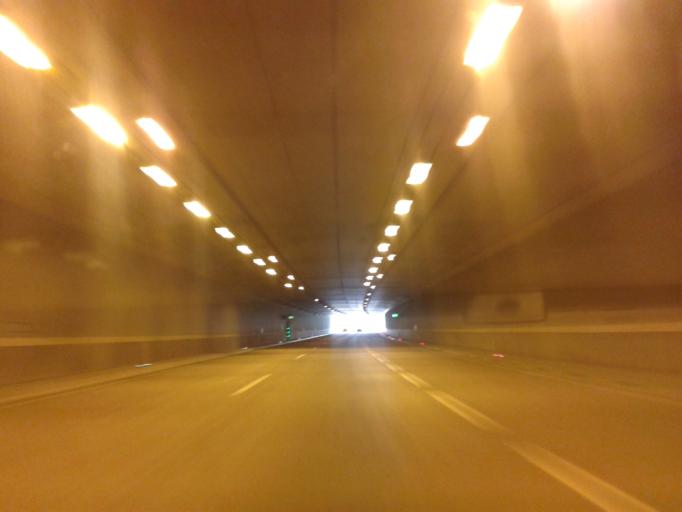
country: AT
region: Lower Austria
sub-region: Politischer Bezirk Wien-Umgebung
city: Leopoldsdorf
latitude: 48.1273
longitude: 16.3874
